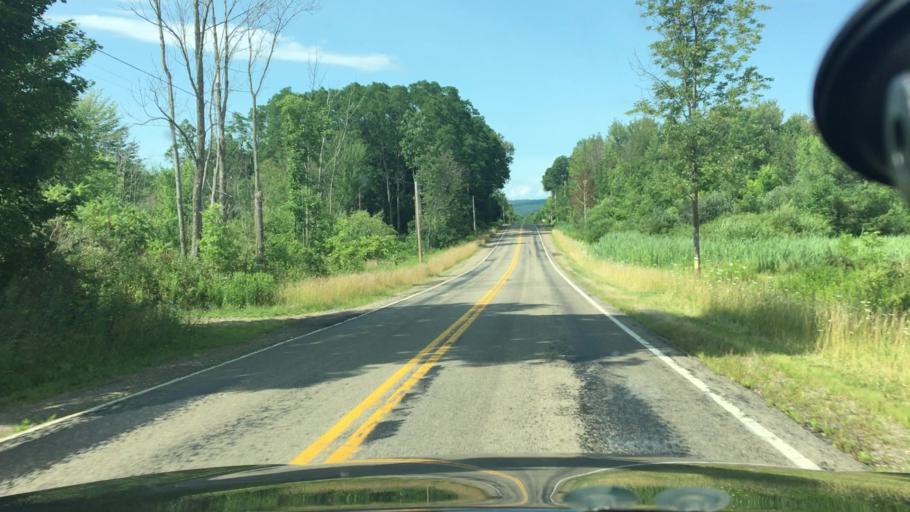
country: US
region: New York
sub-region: Chautauqua County
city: Lakewood
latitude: 42.2426
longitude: -79.3583
